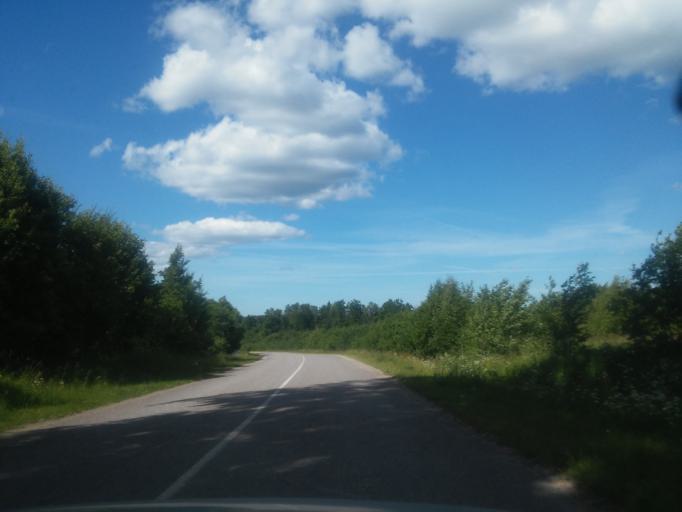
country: LV
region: Skrunda
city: Skrunda
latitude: 56.5920
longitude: 21.9024
